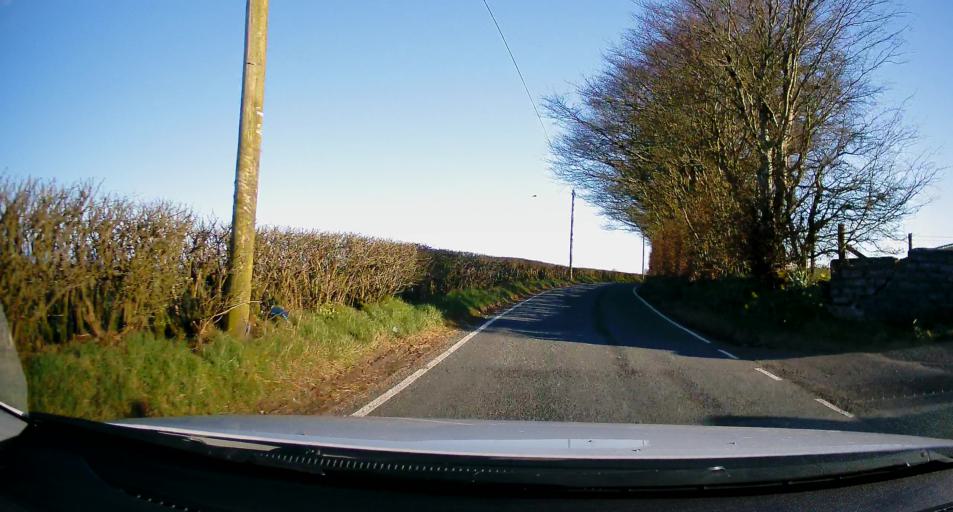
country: GB
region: Wales
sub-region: County of Ceredigion
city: Lledrod
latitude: 52.2652
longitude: -4.0715
